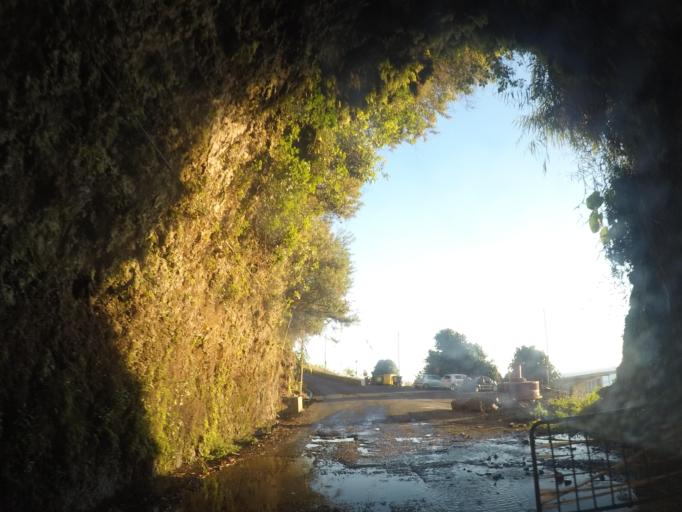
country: PT
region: Madeira
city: Ponta do Sol
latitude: 32.6933
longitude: -17.1173
